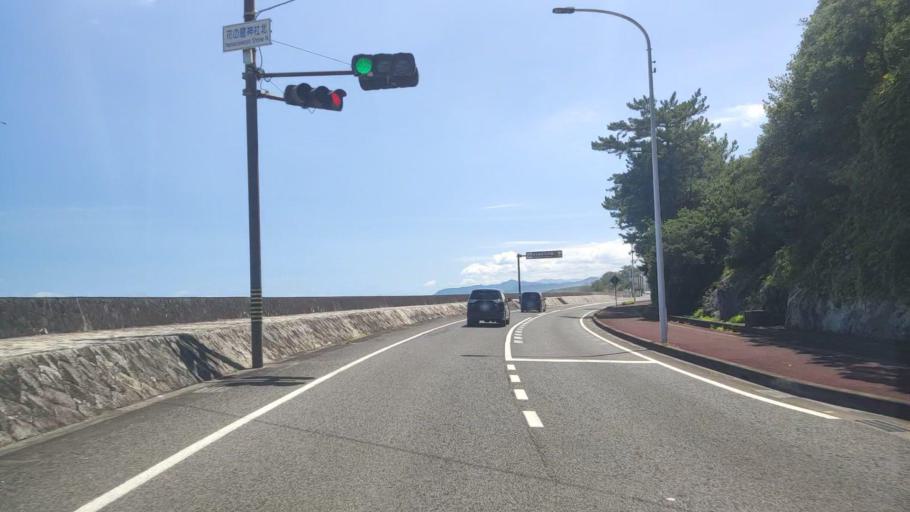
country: JP
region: Wakayama
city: Shingu
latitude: 33.8798
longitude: 136.0941
